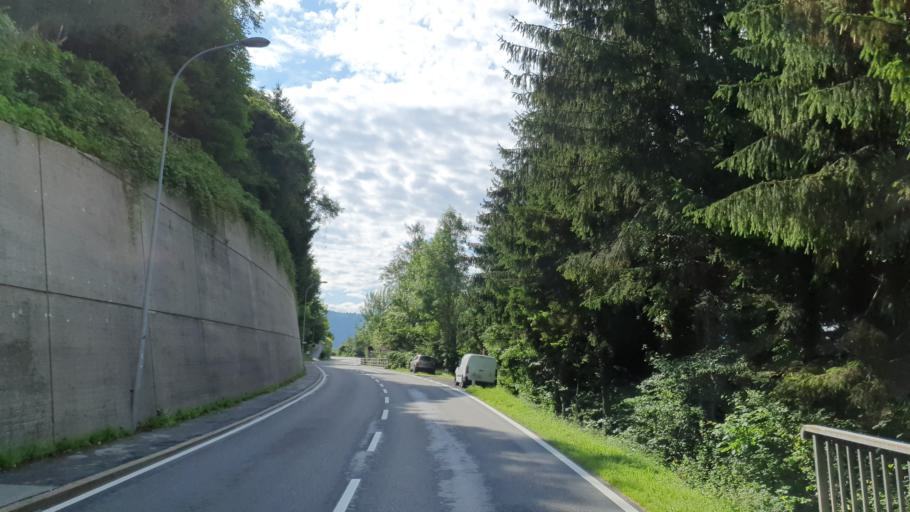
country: AT
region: Vorarlberg
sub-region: Politischer Bezirk Bregenz
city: Bregenz
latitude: 47.4879
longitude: 9.7479
